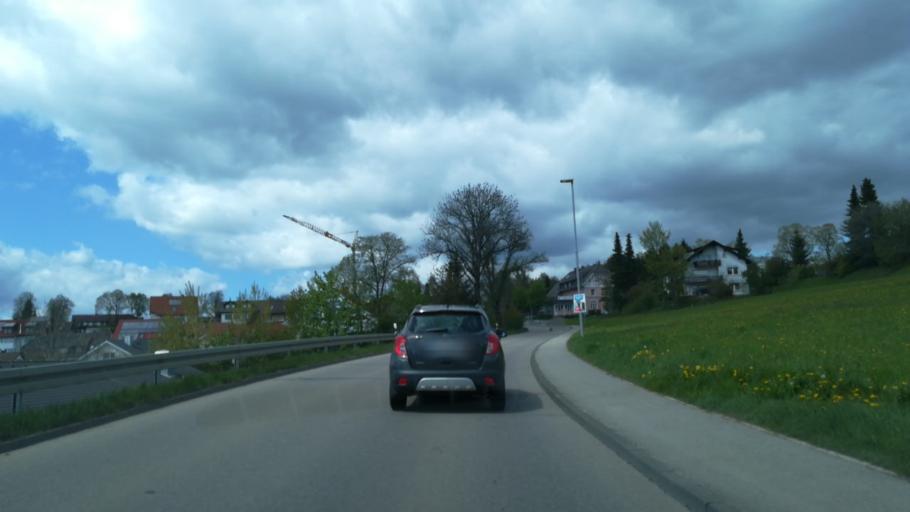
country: DE
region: Baden-Wuerttemberg
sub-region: Freiburg Region
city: Bonndorf im Schwarzwald
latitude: 47.8187
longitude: 8.3475
